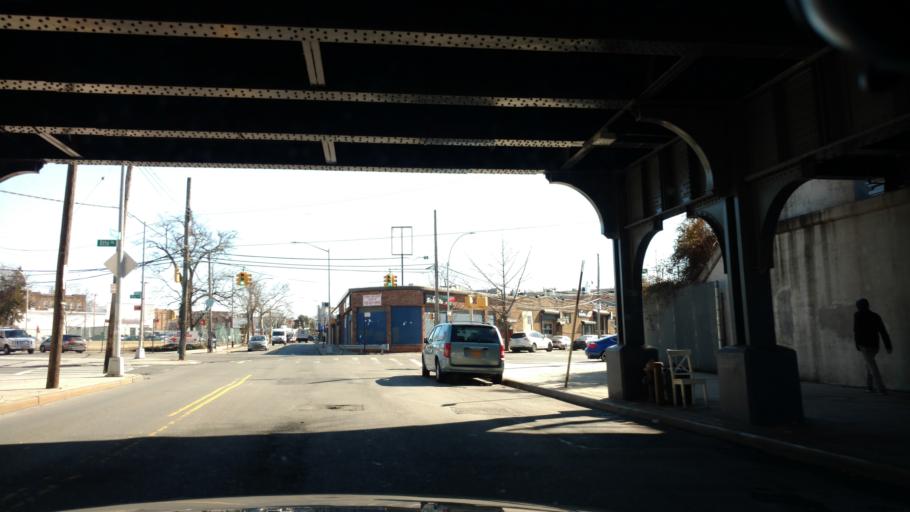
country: US
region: New York
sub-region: Kings County
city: East New York
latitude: 40.7021
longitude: -73.8932
